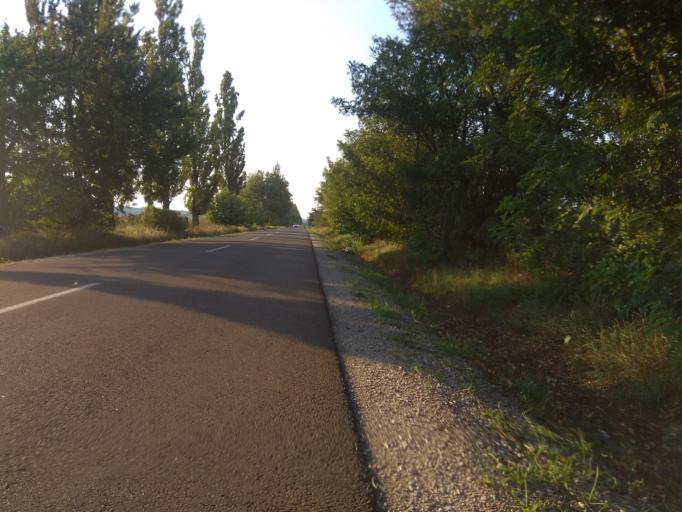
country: HU
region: Borsod-Abauj-Zemplen
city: Nyekladhaza
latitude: 47.9749
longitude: 20.8496
